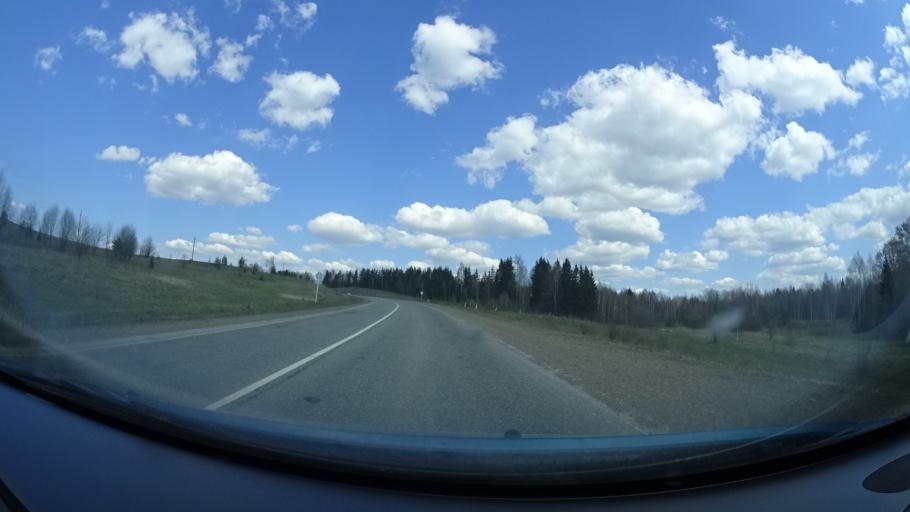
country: RU
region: Perm
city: Osa
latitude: 57.3968
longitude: 55.6213
